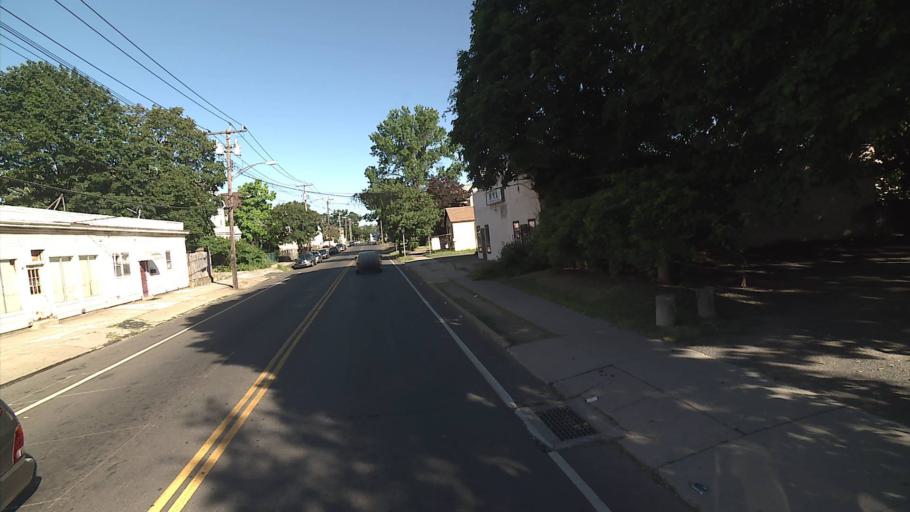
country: US
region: Connecticut
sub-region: New Haven County
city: West Haven
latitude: 41.2792
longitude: -72.9422
